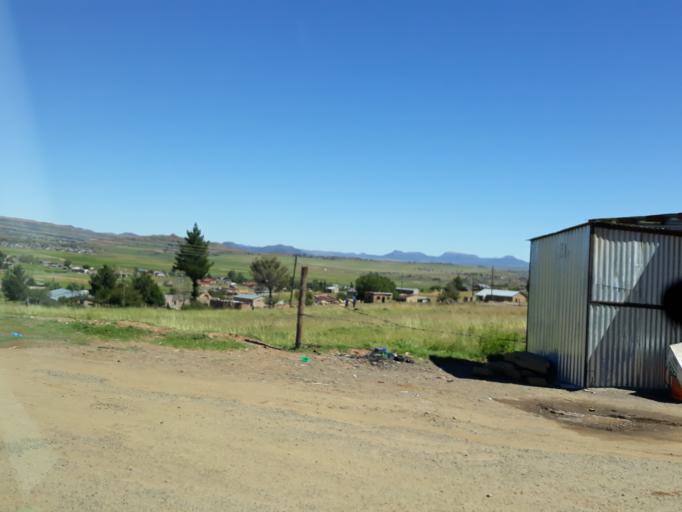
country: LS
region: Mohale's Hoek District
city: Mohale's Hoek
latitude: -30.0998
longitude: 27.4790
